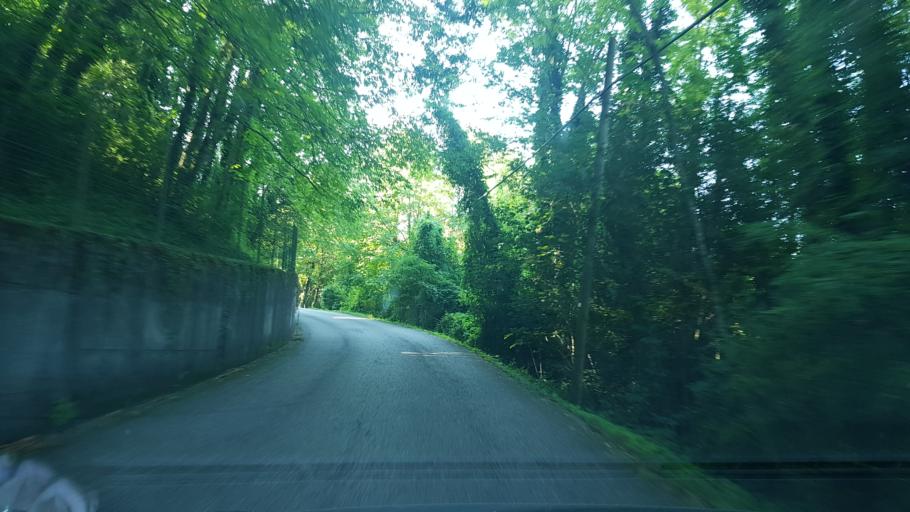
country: IT
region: Friuli Venezia Giulia
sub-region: Provincia di Udine
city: Tarcento
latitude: 46.2144
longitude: 13.2288
